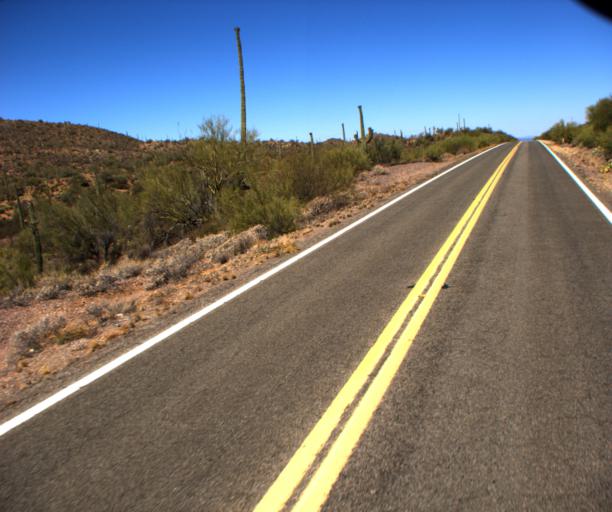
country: US
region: Arizona
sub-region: Pima County
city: Sells
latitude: 32.1741
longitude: -112.1705
